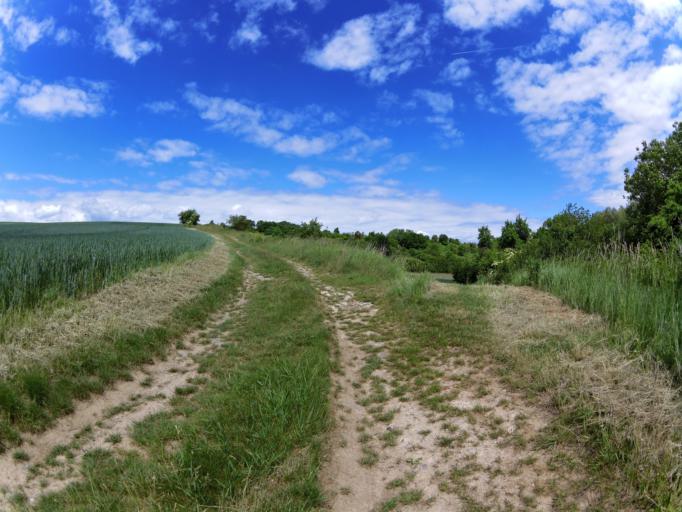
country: DE
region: Bavaria
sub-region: Regierungsbezirk Unterfranken
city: Sommerhausen
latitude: 49.6697
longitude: 10.0141
